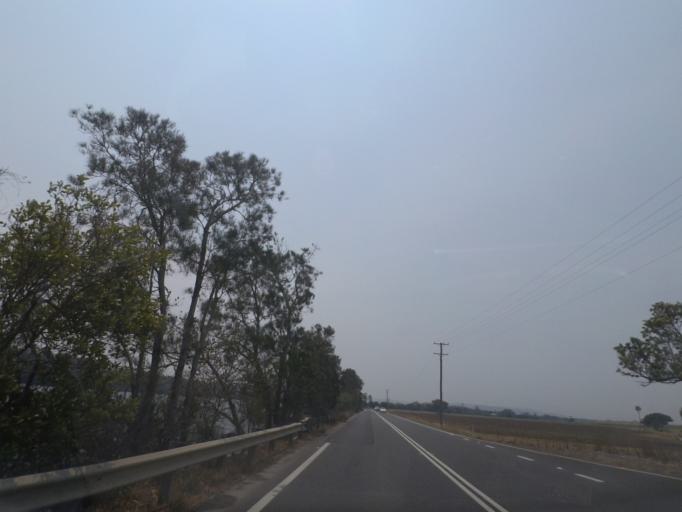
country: AU
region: New South Wales
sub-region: Richmond Valley
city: Evans Head
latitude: -28.9771
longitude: 153.4618
